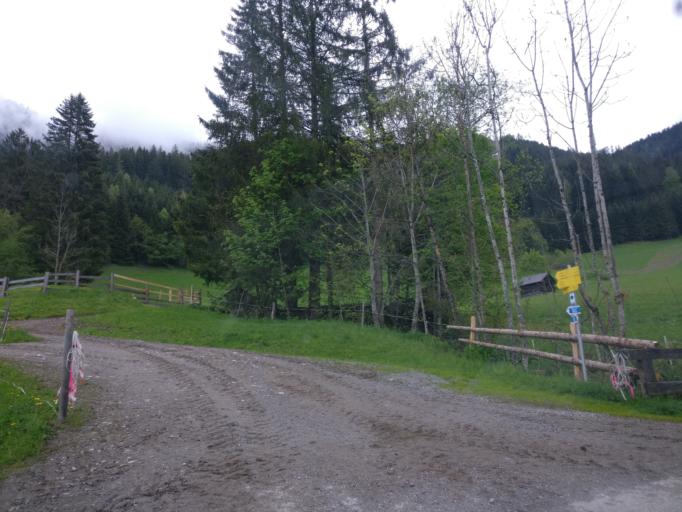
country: AT
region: Salzburg
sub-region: Politischer Bezirk Sankt Johann im Pongau
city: Werfenweng
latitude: 47.4572
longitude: 13.2775
